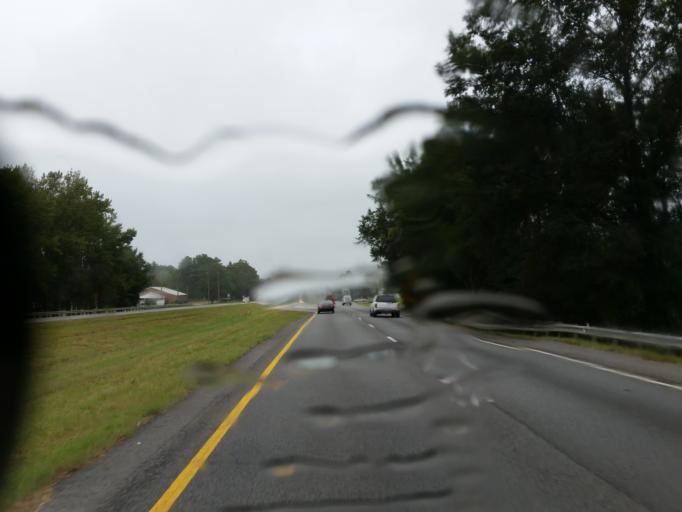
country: US
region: Georgia
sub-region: Spalding County
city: Griffin
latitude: 33.2201
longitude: -84.2888
